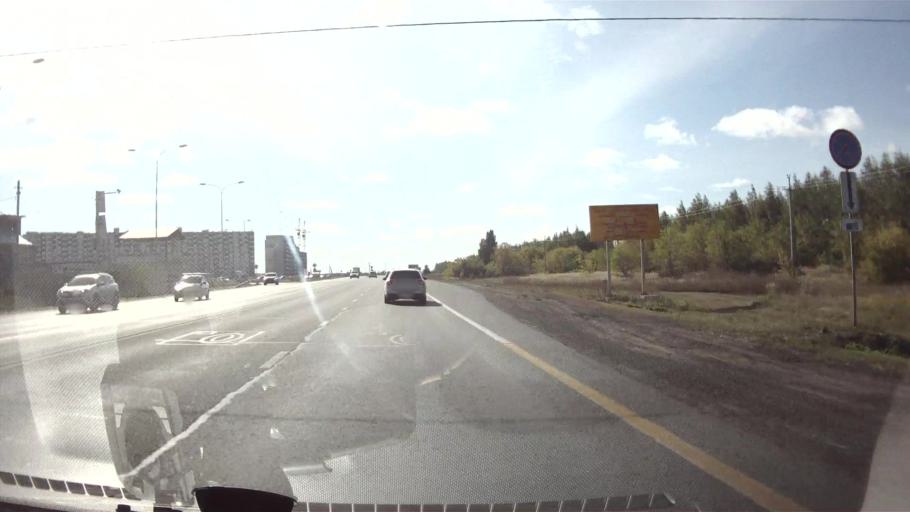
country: RU
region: Ulyanovsk
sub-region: Ulyanovskiy Rayon
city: Ulyanovsk
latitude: 54.2868
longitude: 48.2563
